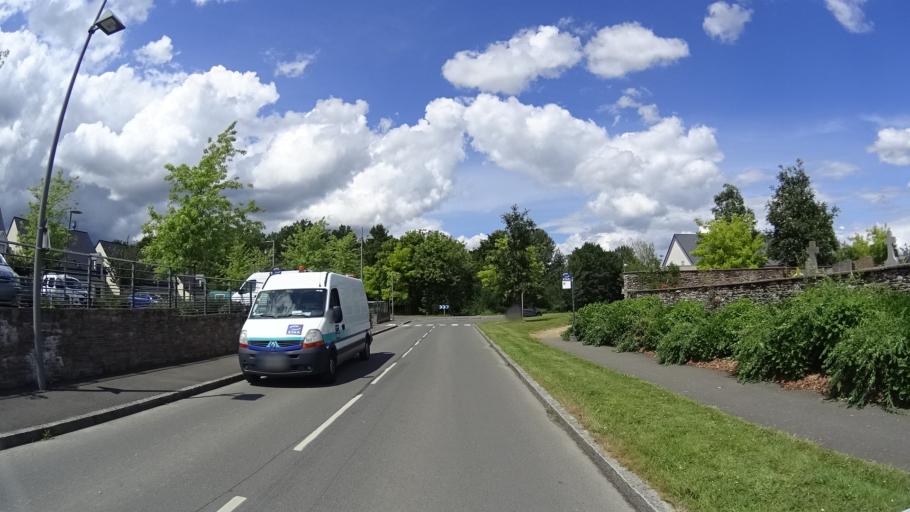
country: FR
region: Brittany
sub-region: Departement d'Ille-et-Vilaine
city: Laille
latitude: 47.9818
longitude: -1.7201
